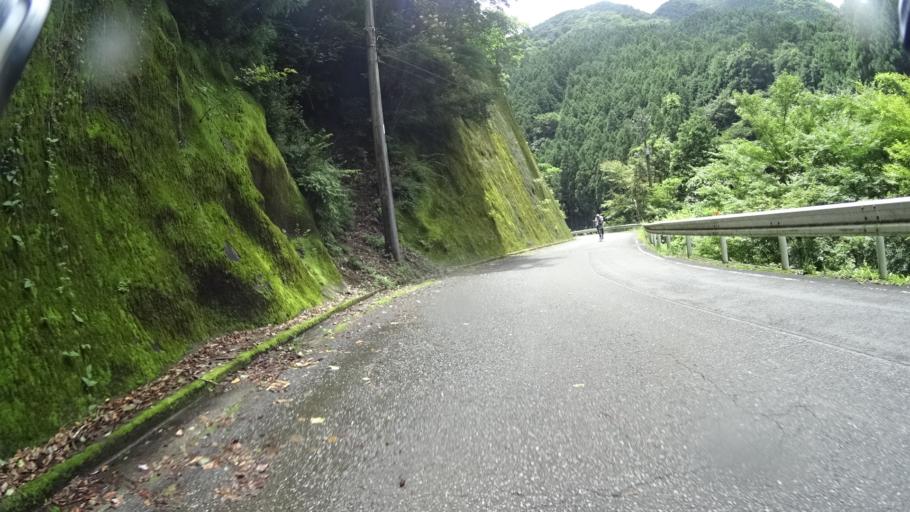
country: JP
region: Tokyo
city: Ome
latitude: 35.8762
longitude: 139.1493
